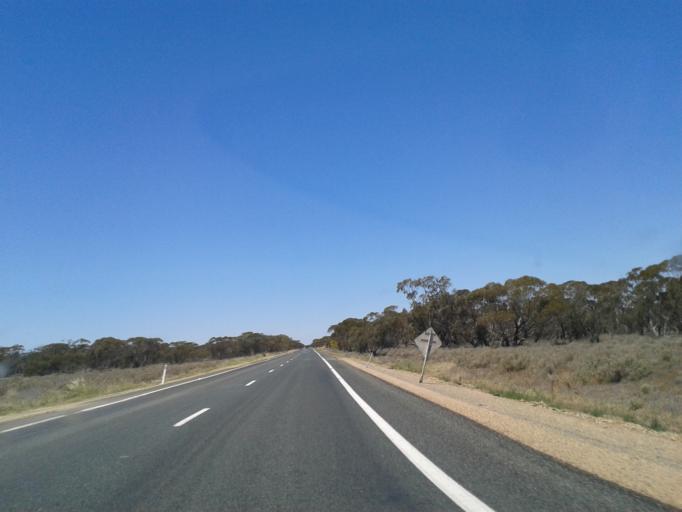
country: AU
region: New South Wales
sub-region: Wentworth
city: Gol Gol
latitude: -34.5192
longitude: 142.6138
